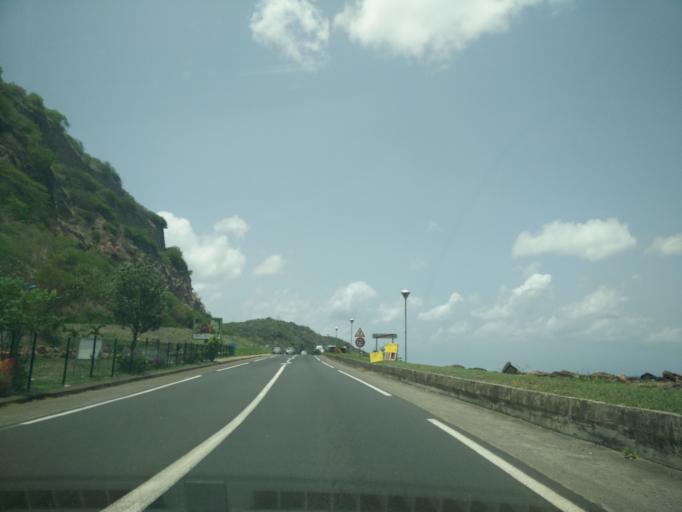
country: MQ
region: Martinique
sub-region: Martinique
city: Saint-Pierre
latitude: 14.6706
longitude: -61.1638
